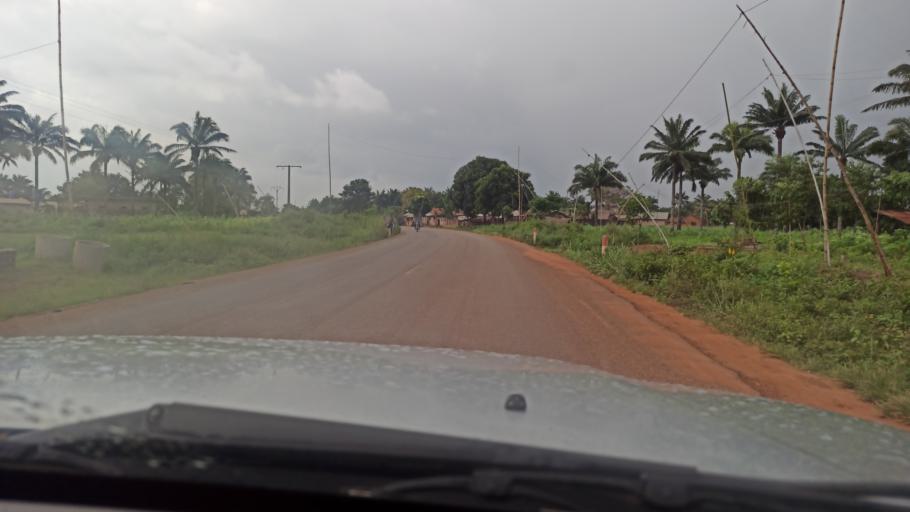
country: BJ
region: Queme
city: Porto-Novo
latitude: 6.5639
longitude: 2.5817
